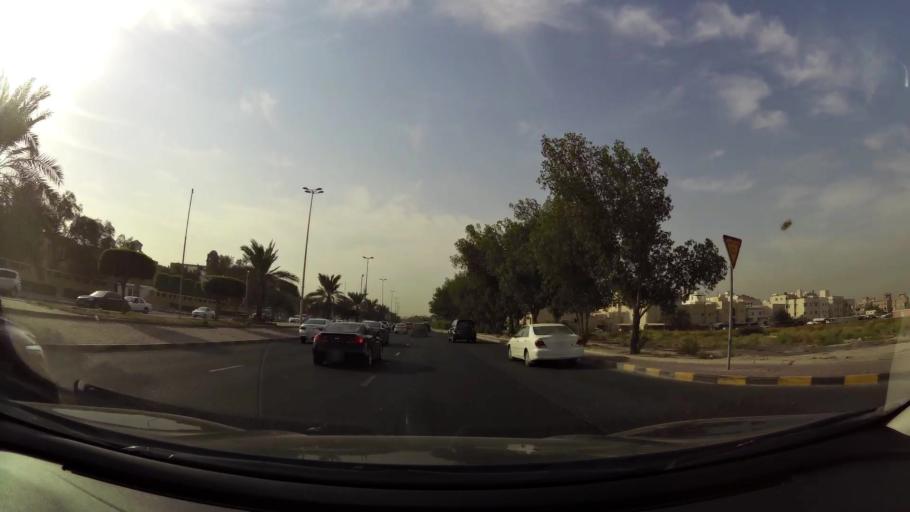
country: KW
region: Muhafazat Hawalli
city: Salwa
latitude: 29.3043
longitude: 48.0852
